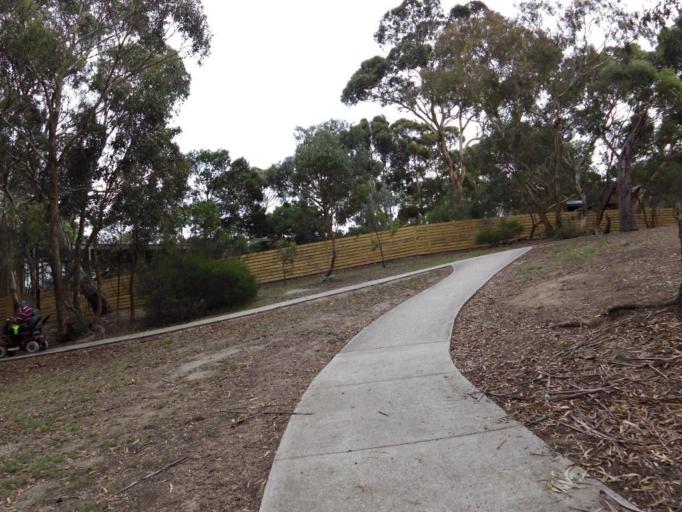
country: AU
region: Victoria
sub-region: Hume
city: Sunbury
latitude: -37.5658
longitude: 144.7220
